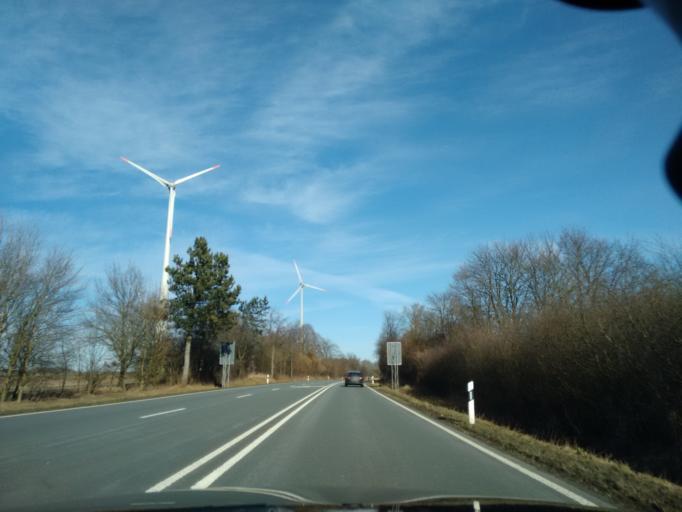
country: DE
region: North Rhine-Westphalia
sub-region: Regierungsbezirk Detmold
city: Altenbeken
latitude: 51.7333
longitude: 8.9212
